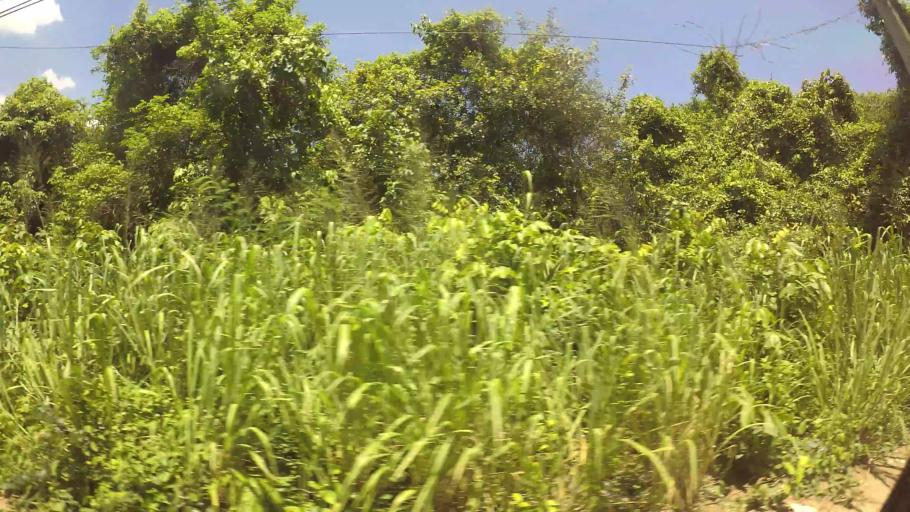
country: TH
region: Chon Buri
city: Si Racha
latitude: 13.1386
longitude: 100.9572
